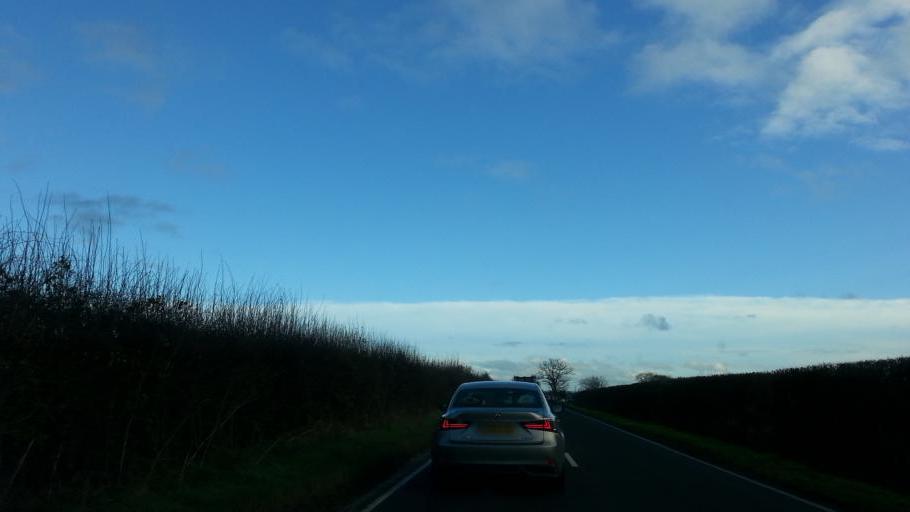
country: GB
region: England
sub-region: Oxfordshire
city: Shrivenham
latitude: 51.6147
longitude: -1.6212
